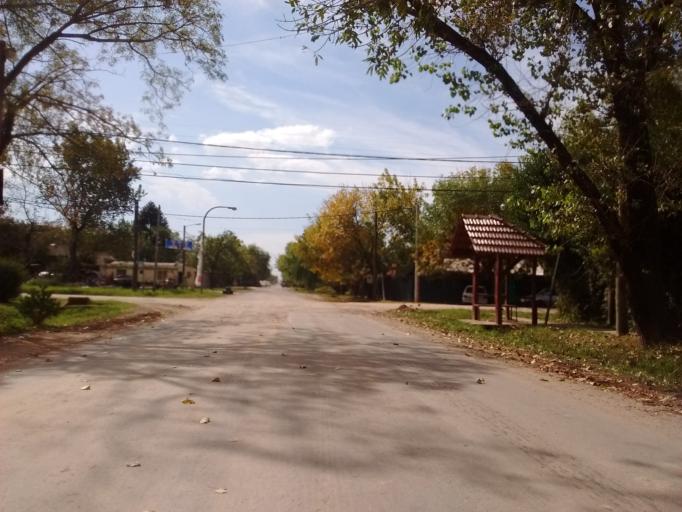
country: AR
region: Santa Fe
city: Funes
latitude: -32.9077
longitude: -60.8132
